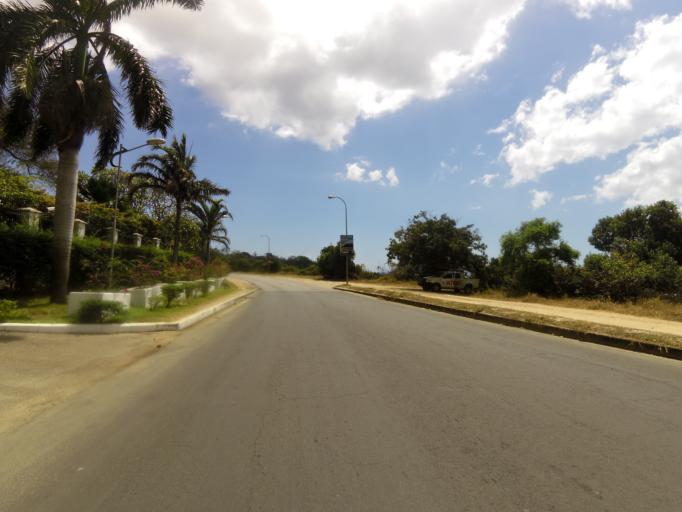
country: TZ
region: Dar es Salaam
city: Magomeni
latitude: -6.7906
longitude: 39.2803
